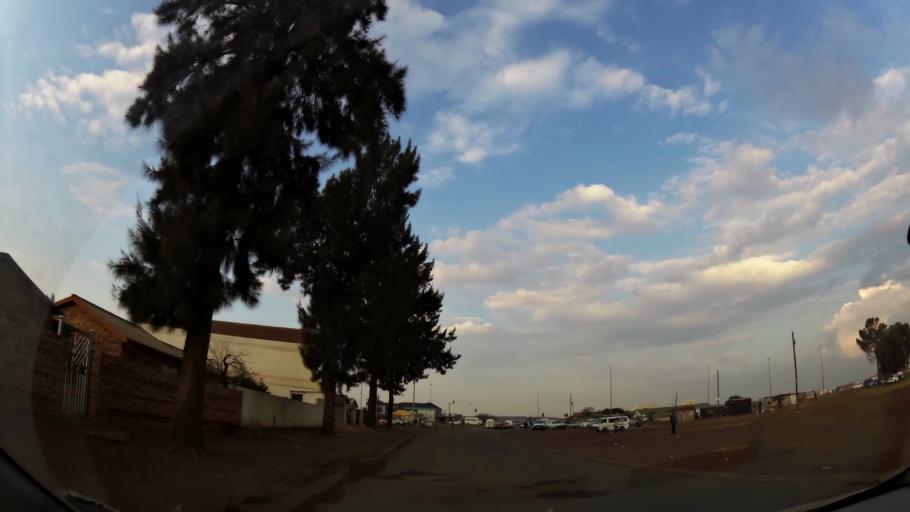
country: ZA
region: Gauteng
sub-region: City of Johannesburg Metropolitan Municipality
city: Orange Farm
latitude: -26.5931
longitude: 27.8457
